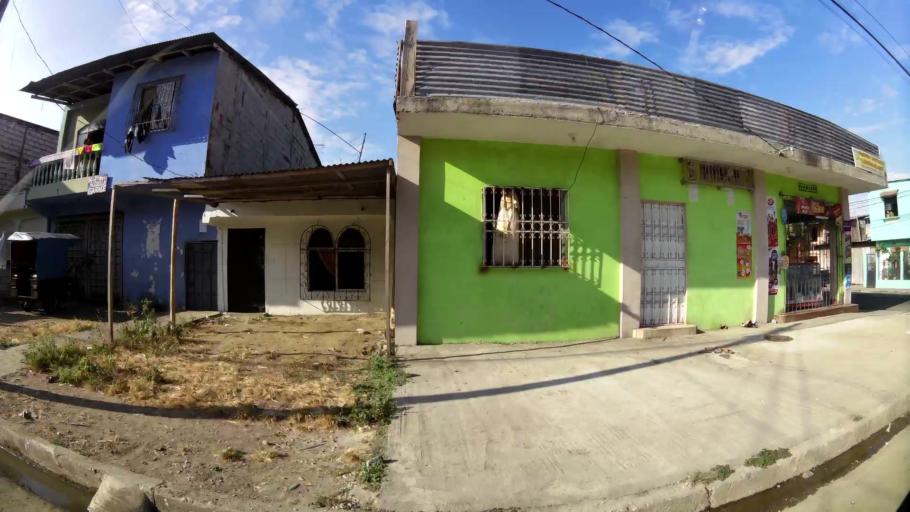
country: EC
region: Guayas
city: Guayaquil
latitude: -2.2198
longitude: -79.9173
